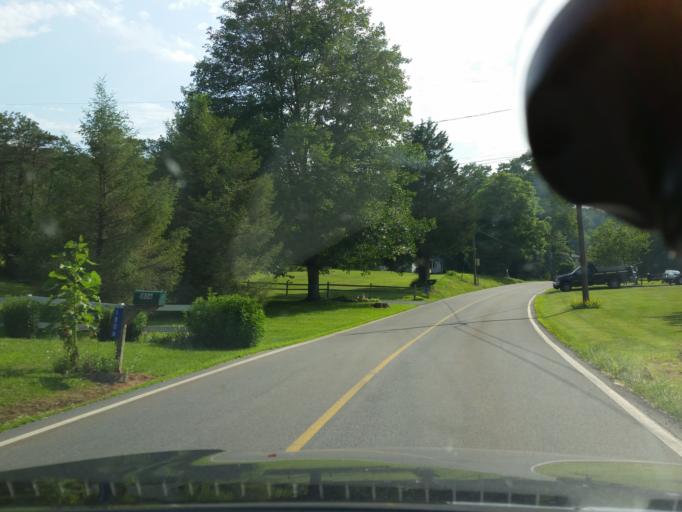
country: US
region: Pennsylvania
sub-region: Perry County
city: Marysville
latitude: 40.3245
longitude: -76.9894
